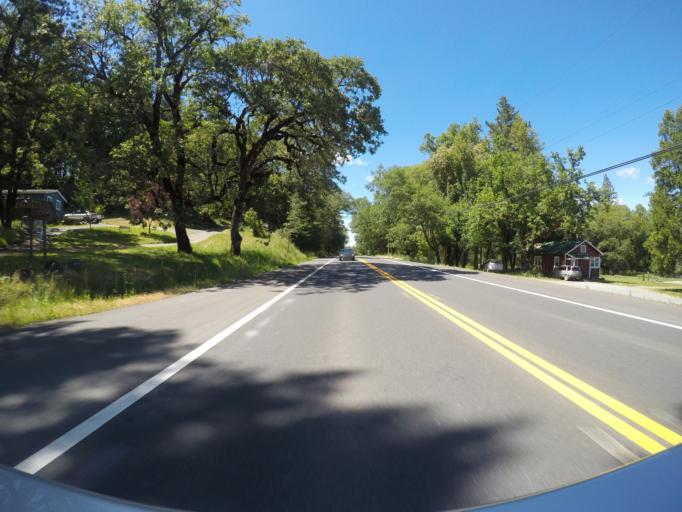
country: US
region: California
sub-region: Mendocino County
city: Laytonville
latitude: 39.6442
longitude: -123.4745
